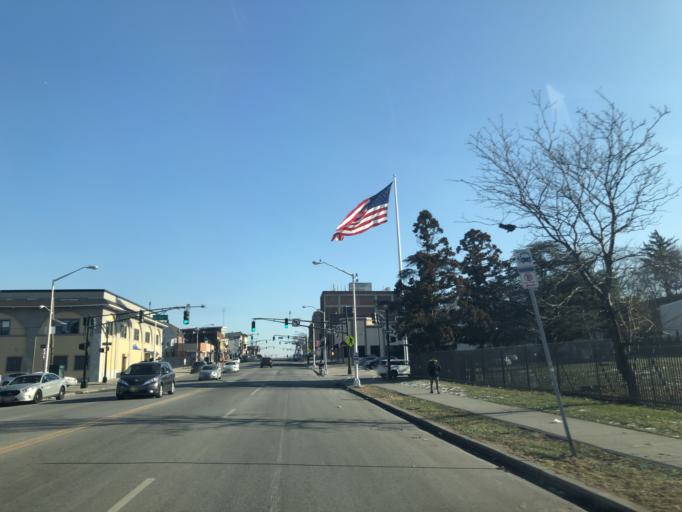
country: US
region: New Jersey
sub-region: Essex County
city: East Orange
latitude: 40.7497
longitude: -74.1989
